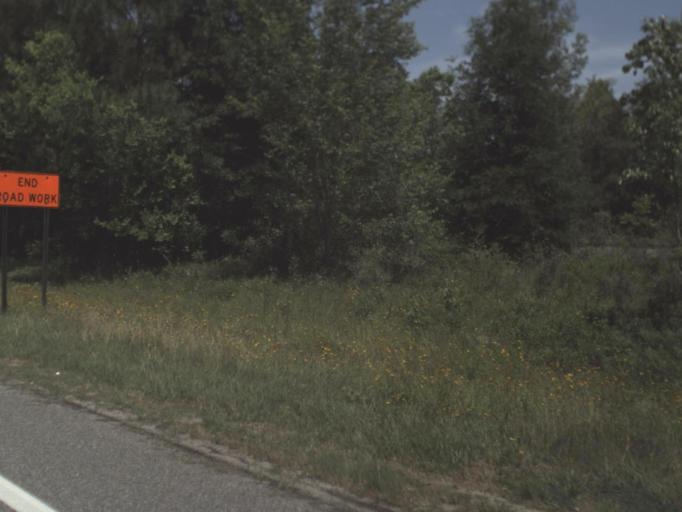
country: US
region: Florida
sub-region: Suwannee County
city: Live Oak
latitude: 30.3484
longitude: -83.1012
